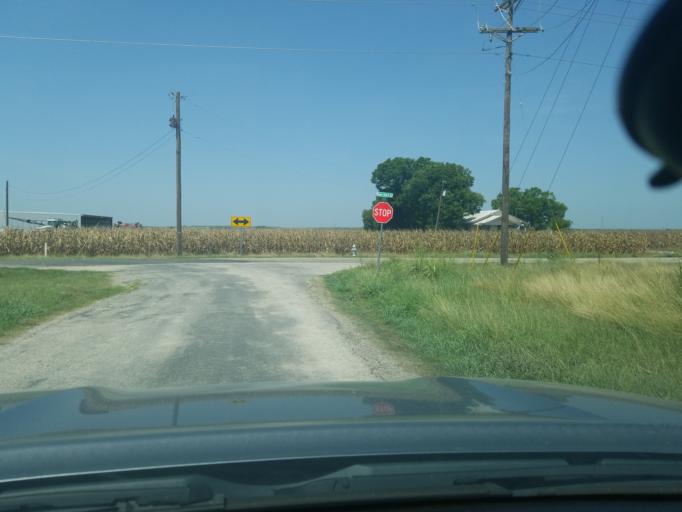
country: US
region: Texas
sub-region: Guadalupe County
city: Lake Dunlap
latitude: 29.6866
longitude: -98.0354
